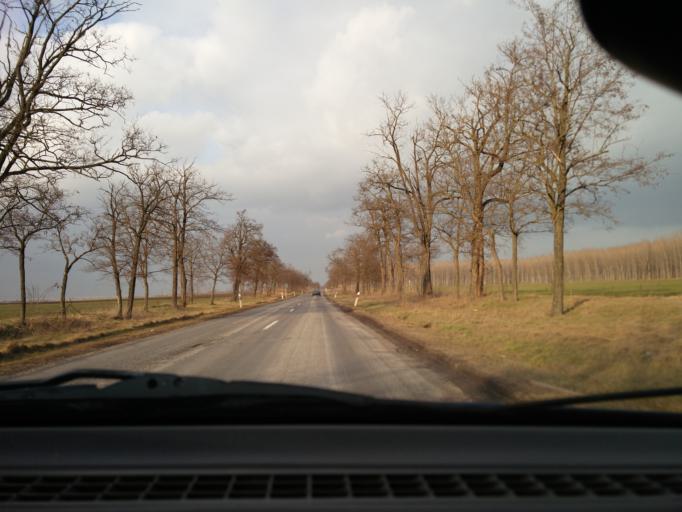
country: HU
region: Pest
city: Tapioszolos
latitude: 47.2987
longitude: 19.8692
